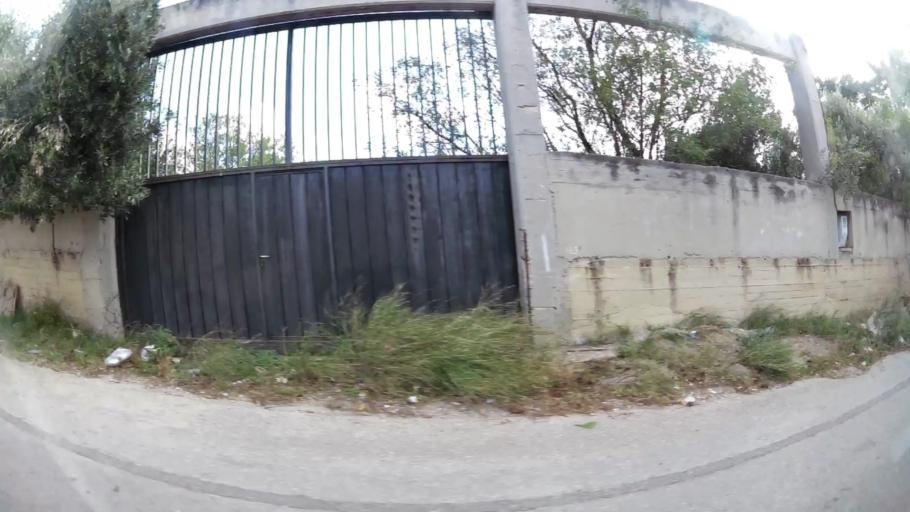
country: GR
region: Attica
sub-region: Nomarchia Anatolikis Attikis
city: Thrakomakedones
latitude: 38.1102
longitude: 23.7573
